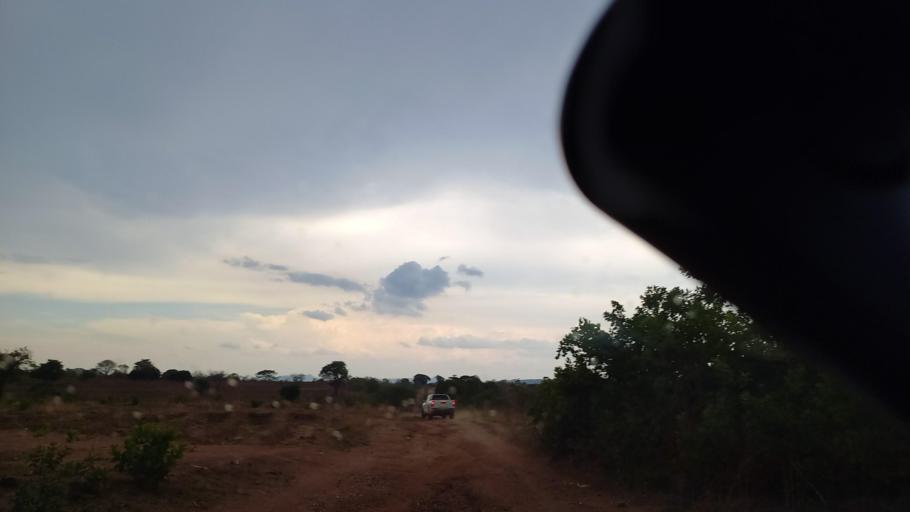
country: ZM
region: Lusaka
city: Kafue
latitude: -15.9900
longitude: 28.2704
